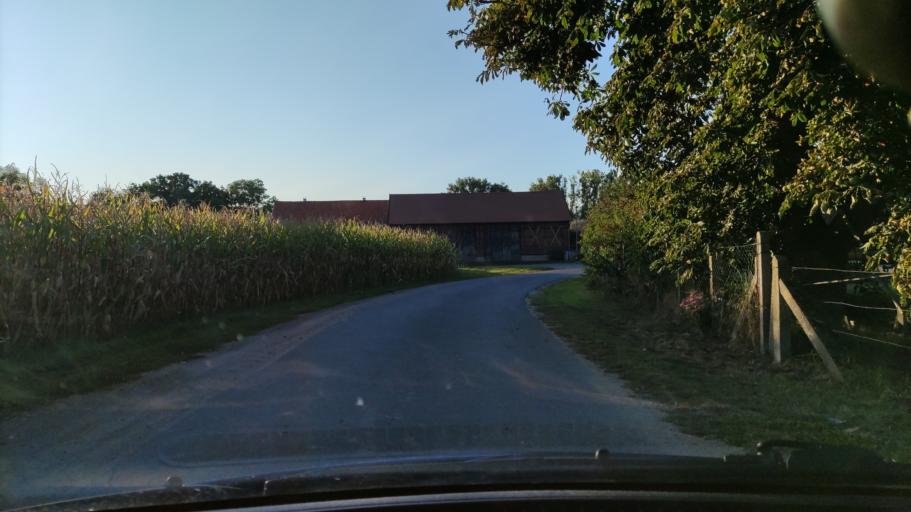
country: DE
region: Lower Saxony
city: Dannenberg
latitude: 53.1206
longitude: 11.1013
